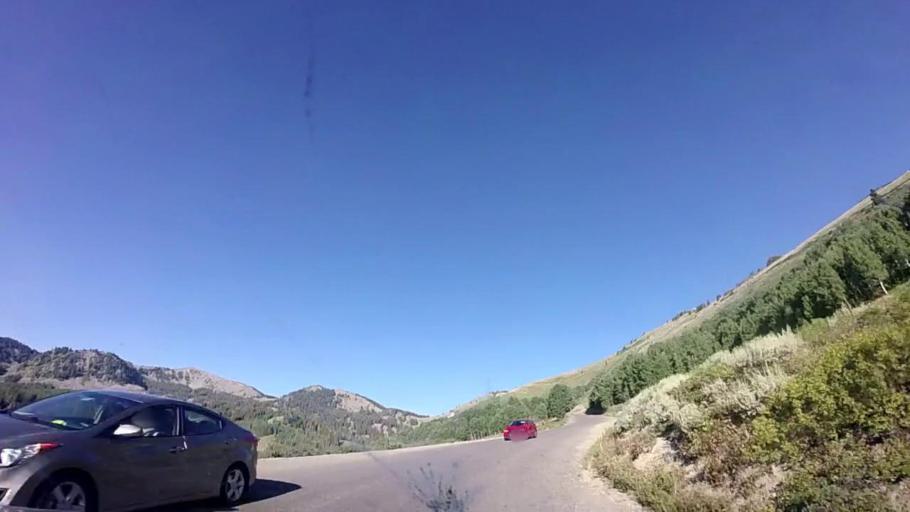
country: US
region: Utah
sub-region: Summit County
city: Park City
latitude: 40.6090
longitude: -111.5304
